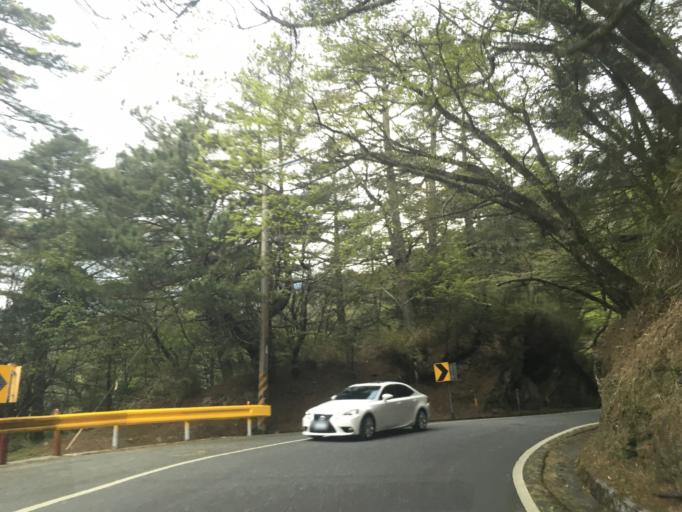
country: TW
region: Taiwan
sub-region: Hualien
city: Hualian
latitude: 24.1800
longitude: 121.3160
